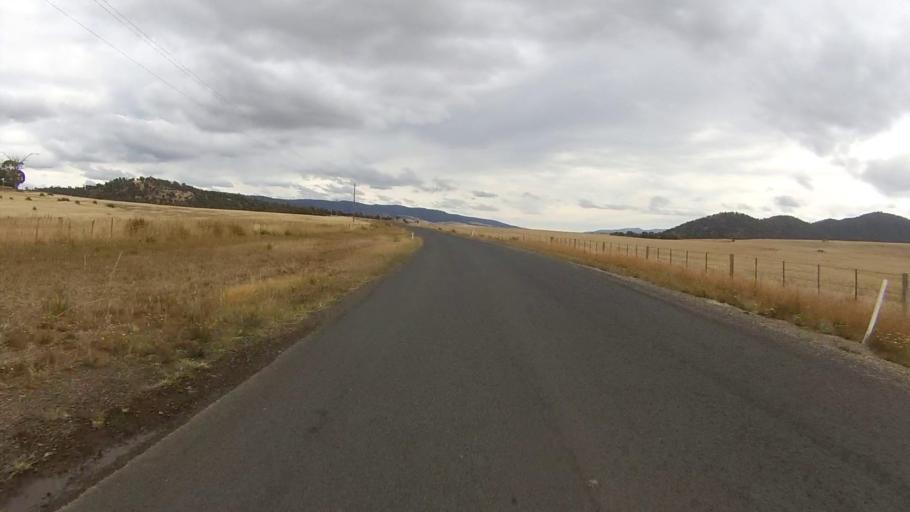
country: AU
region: Tasmania
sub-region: Northern Midlands
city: Evandale
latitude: -41.8238
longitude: 147.8132
